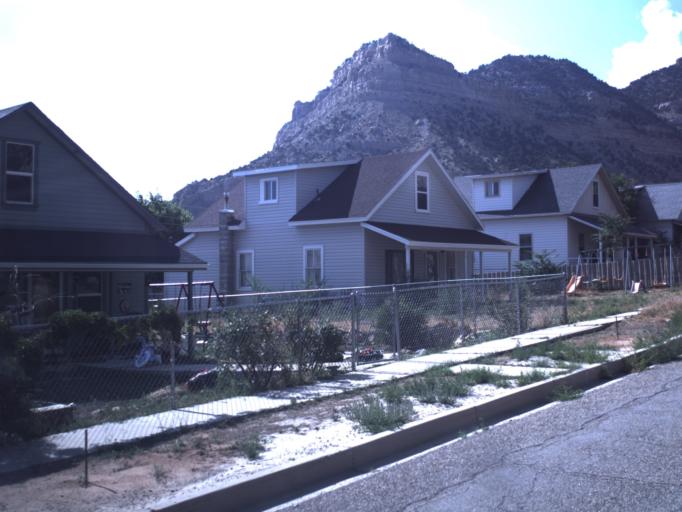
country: US
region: Utah
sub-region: Carbon County
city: Helper
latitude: 39.6863
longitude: -110.8039
